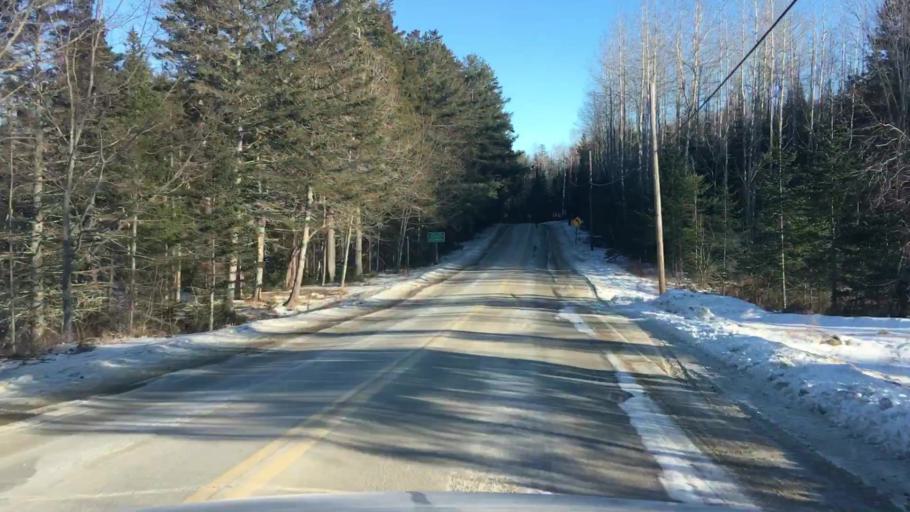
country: US
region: Maine
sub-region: Hancock County
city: Penobscot
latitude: 44.3979
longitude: -68.7032
